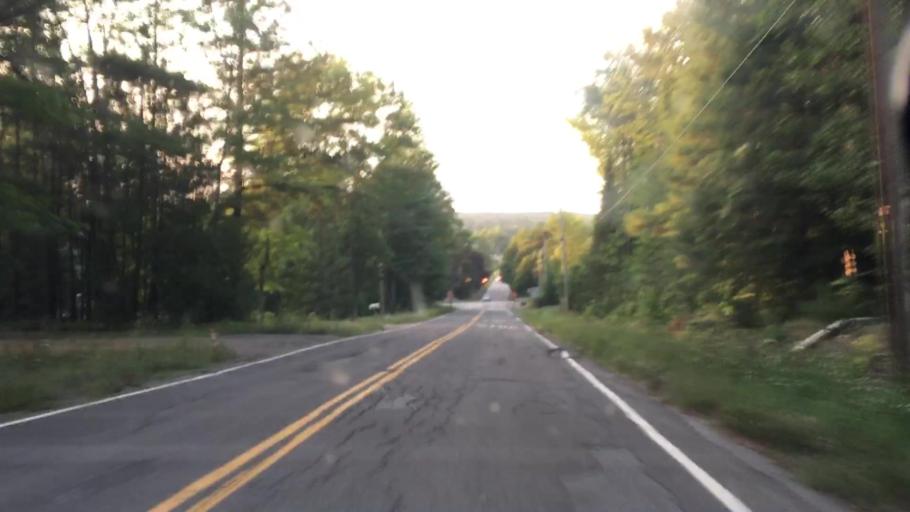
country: US
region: Maine
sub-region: Penobscot County
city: Hermon
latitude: 44.7336
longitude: -68.9630
